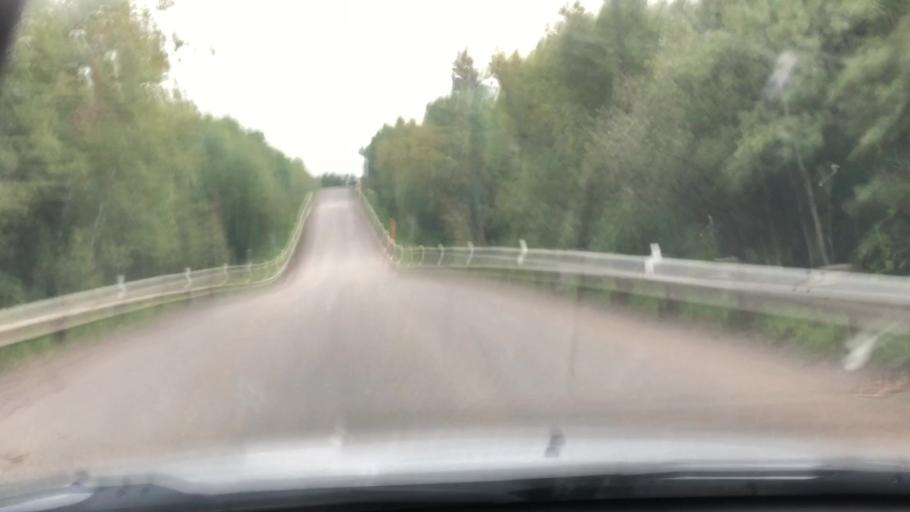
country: CA
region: Alberta
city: Devon
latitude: 53.4278
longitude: -113.6769
